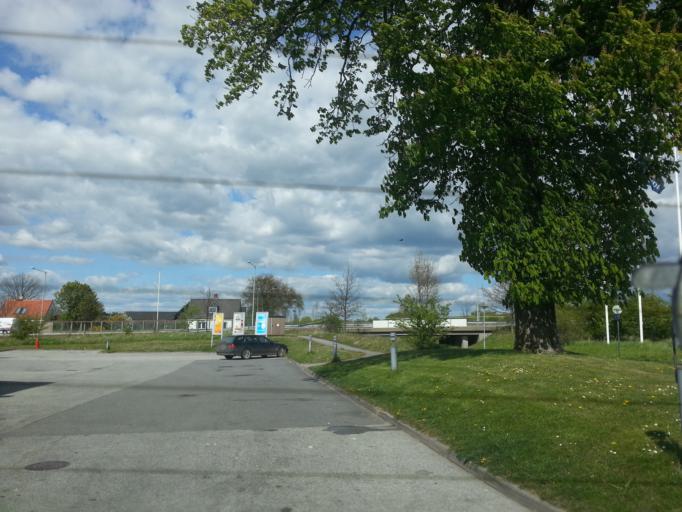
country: SE
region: Skane
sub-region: Ystads Kommun
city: Ystad
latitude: 55.4382
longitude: 13.7914
